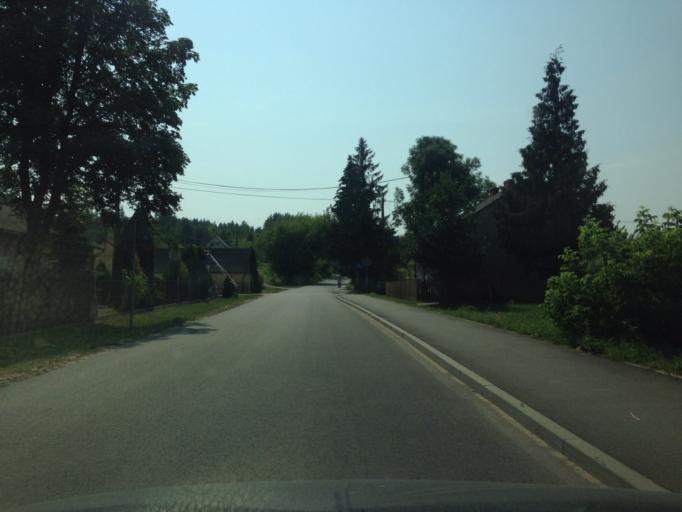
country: PL
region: Kujawsko-Pomorskie
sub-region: Powiat golubsko-dobrzynski
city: Golub-Dobrzyn
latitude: 53.0777
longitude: 19.0311
